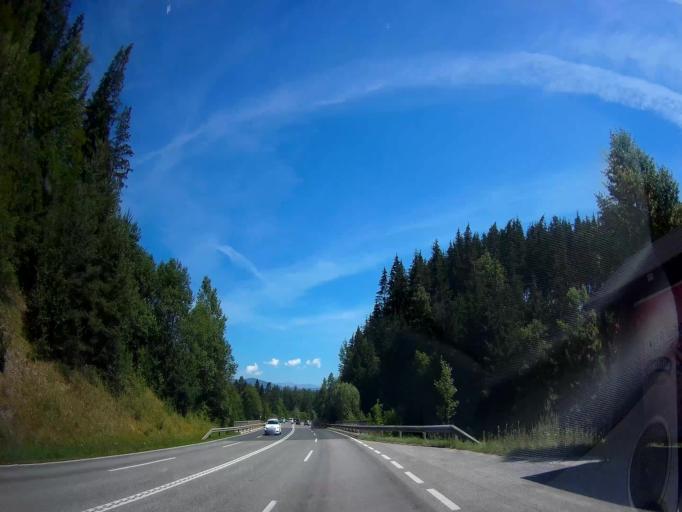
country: AT
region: Carinthia
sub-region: Politischer Bezirk Sankt Veit an der Glan
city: Molbling
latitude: 46.8161
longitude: 14.4311
